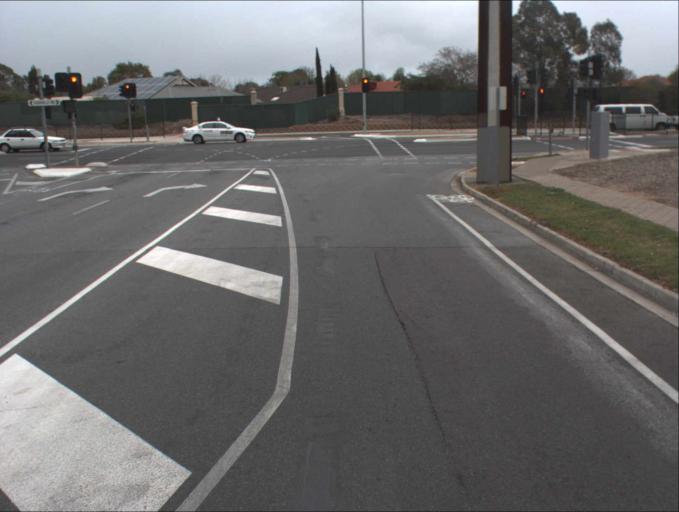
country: AU
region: South Australia
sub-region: Port Adelaide Enfield
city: Gilles Plains
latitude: -34.8552
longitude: 138.6537
